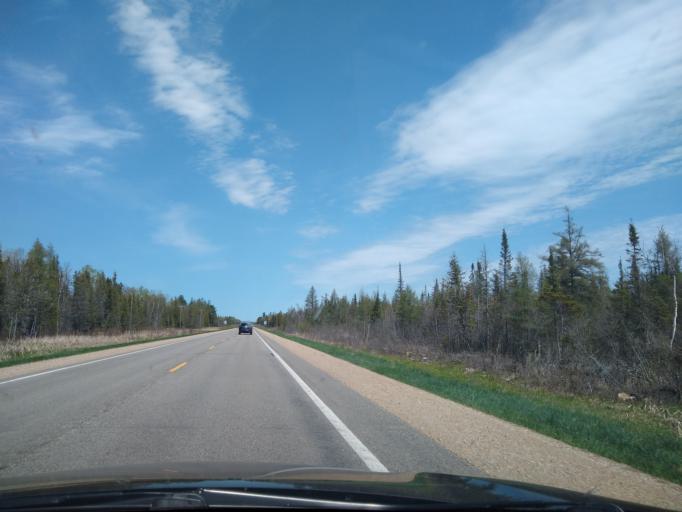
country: US
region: Michigan
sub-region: Delta County
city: Gladstone
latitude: 45.9529
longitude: -86.9720
